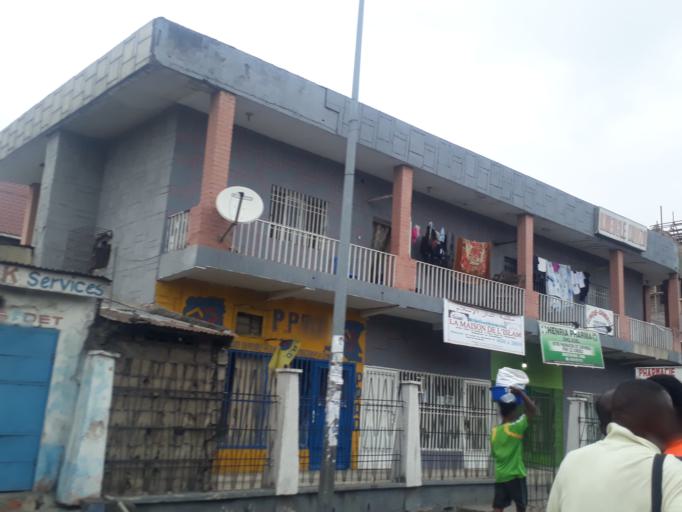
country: CD
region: Kinshasa
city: Kinshasa
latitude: -4.3197
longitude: 15.3112
